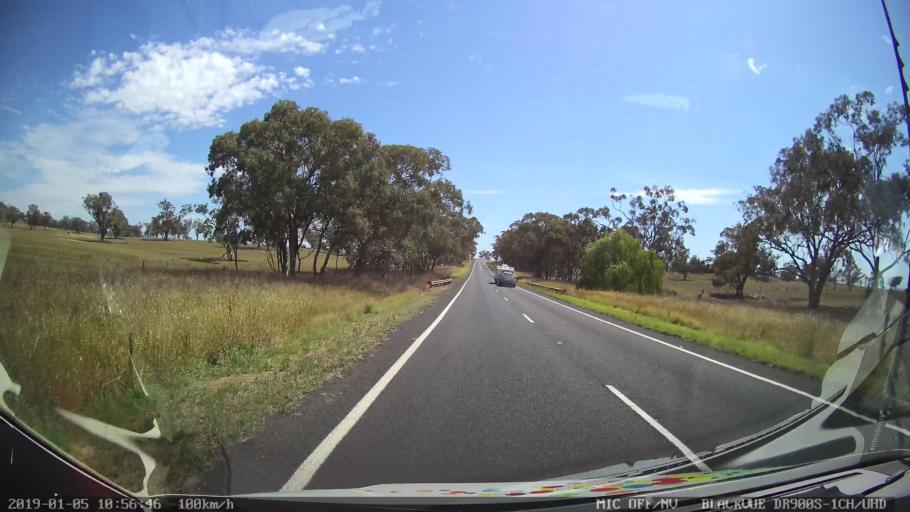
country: AU
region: New South Wales
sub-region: Warrumbungle Shire
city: Coonabarabran
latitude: -31.4379
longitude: 149.1616
